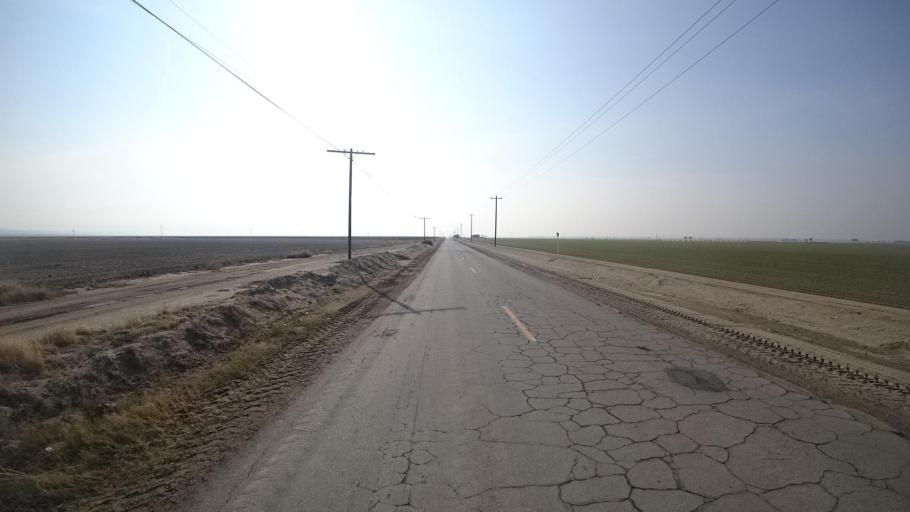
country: US
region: California
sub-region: Kern County
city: Arvin
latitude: 35.0804
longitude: -118.8465
